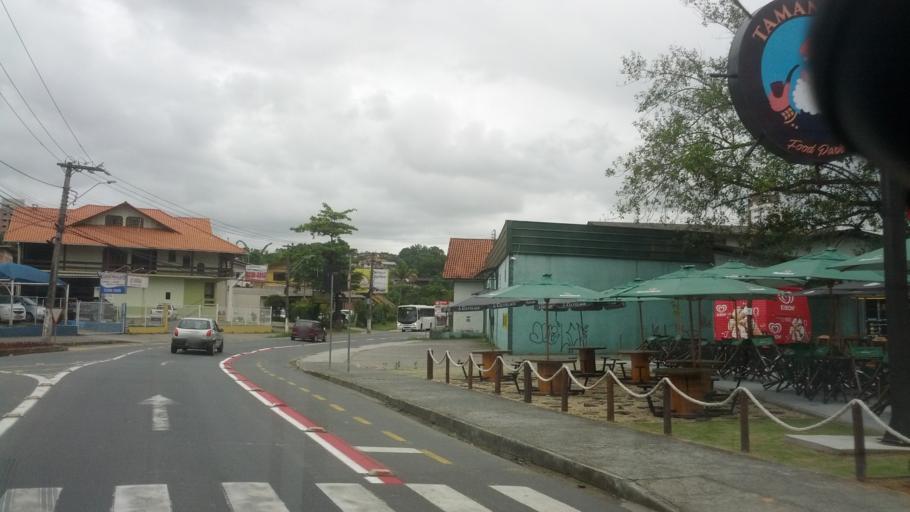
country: BR
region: Santa Catarina
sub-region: Blumenau
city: Blumenau
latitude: -26.9116
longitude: -49.0859
